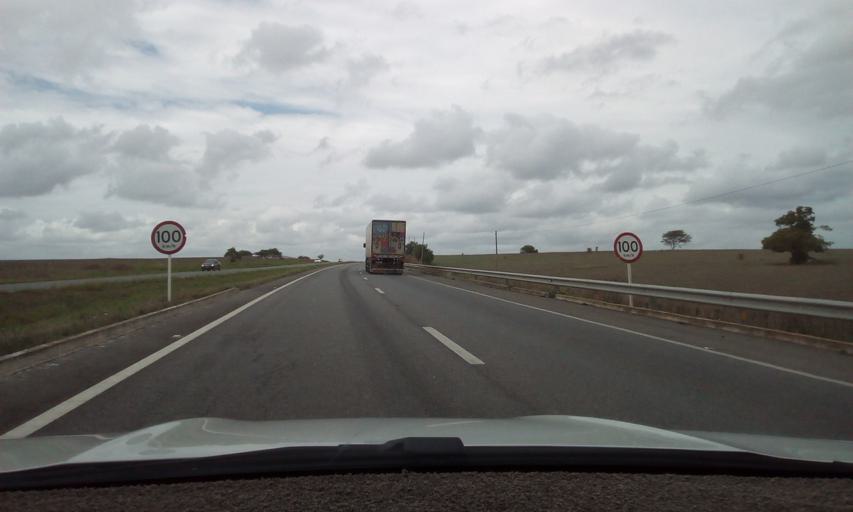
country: BR
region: Paraiba
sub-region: Gurinhem
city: Gurinhem
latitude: -7.1855
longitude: -35.4490
